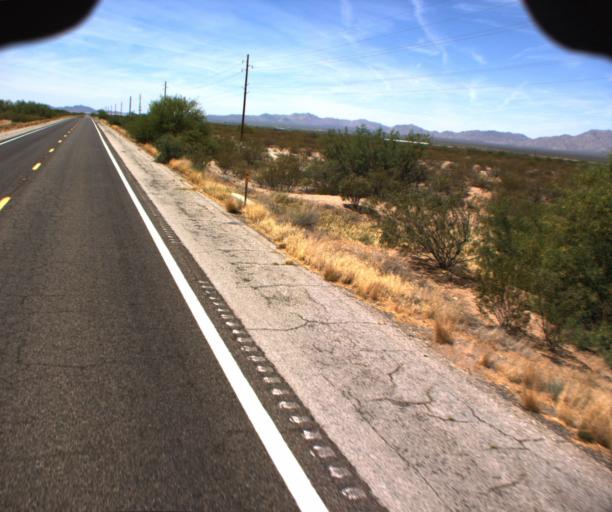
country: US
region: Arizona
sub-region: La Paz County
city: Salome
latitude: 33.8512
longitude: -113.4483
